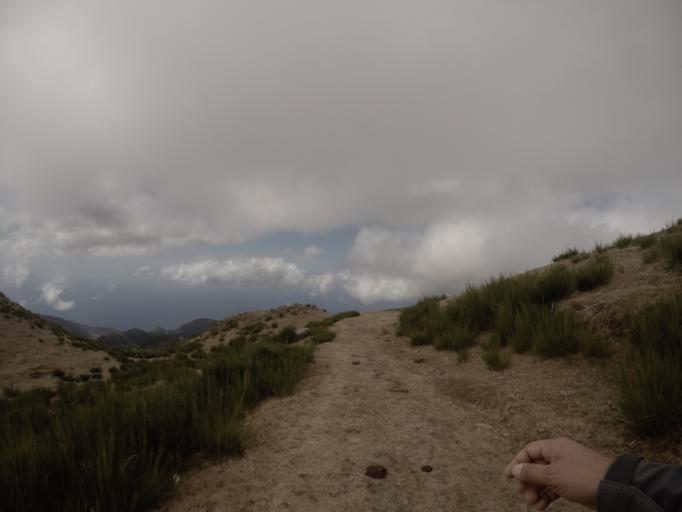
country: PT
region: Madeira
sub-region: Camara de Lobos
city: Curral das Freiras
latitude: 32.7151
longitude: -17.0032
